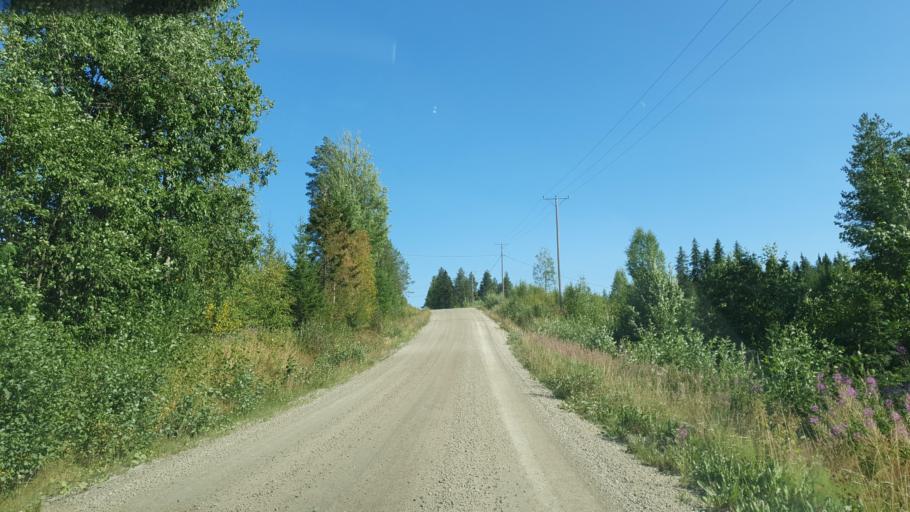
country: FI
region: Kainuu
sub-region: Kehys-Kainuu
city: Kuhmo
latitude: 64.0465
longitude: 29.6498
